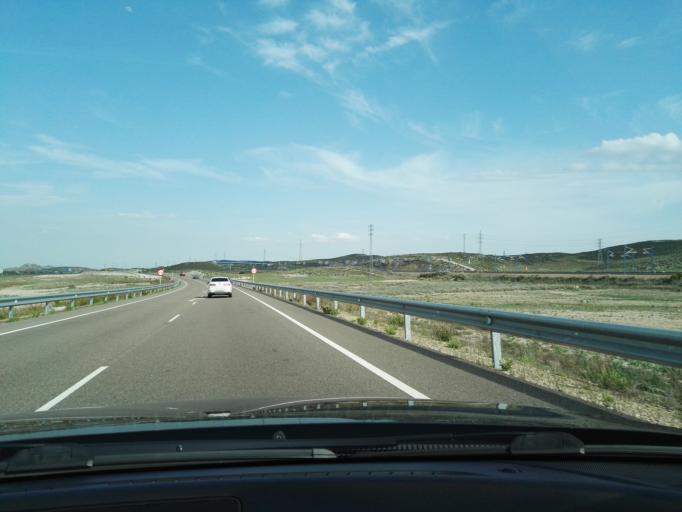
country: ES
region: Aragon
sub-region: Provincia de Zaragoza
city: Montecanal
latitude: 41.6233
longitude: -0.9829
